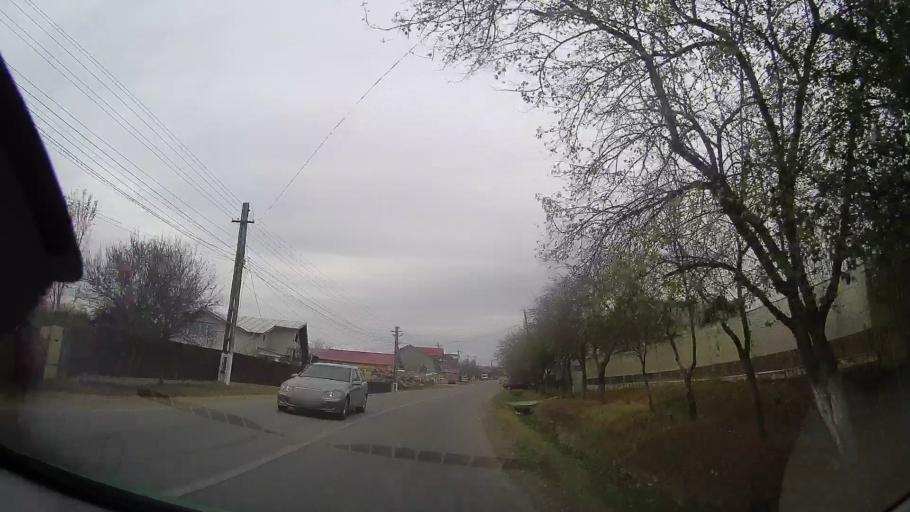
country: RO
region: Prahova
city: Mocesti
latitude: 45.0588
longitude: 26.2430
